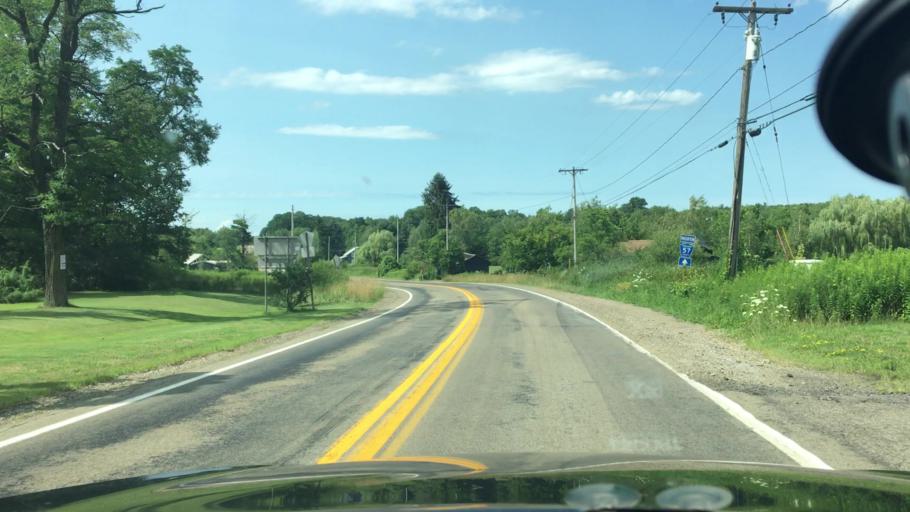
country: US
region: New York
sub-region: Chautauqua County
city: Lakewood
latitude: 42.1837
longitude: -79.3465
